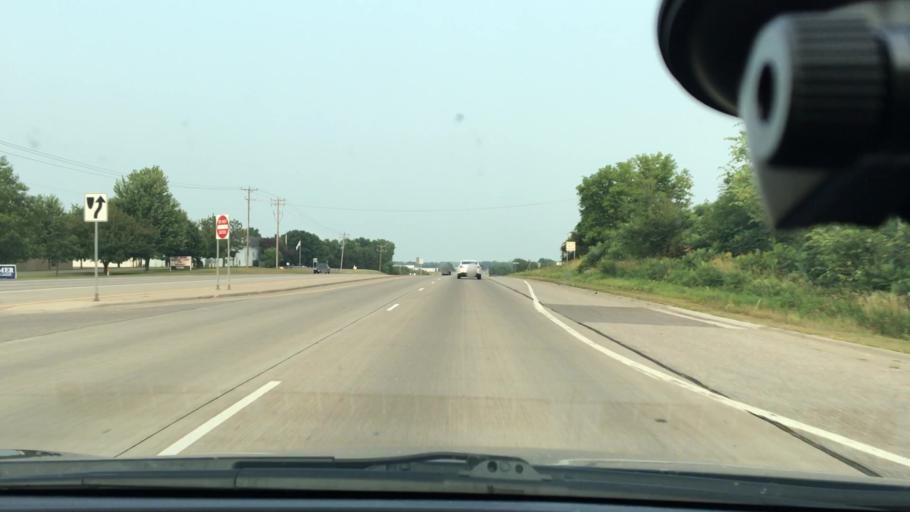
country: US
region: Minnesota
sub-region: Wright County
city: Saint Michael
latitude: 45.2111
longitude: -93.6393
